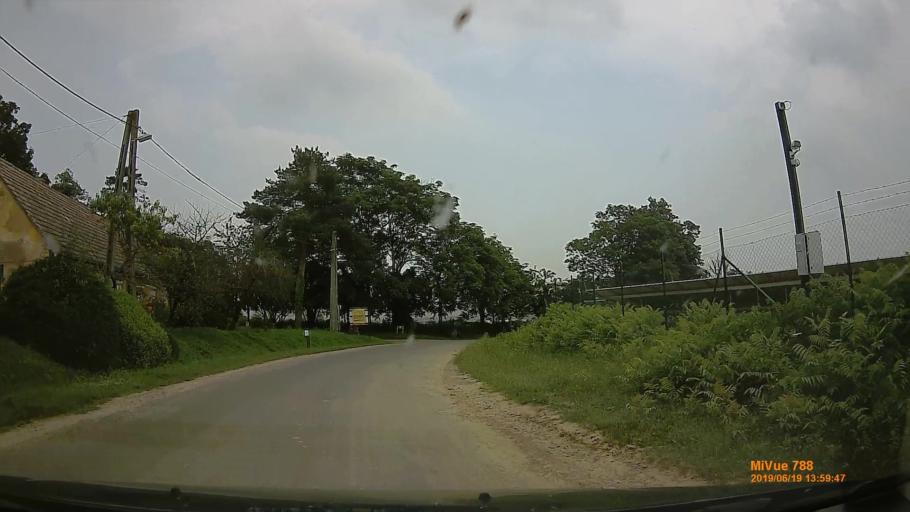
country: HU
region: Baranya
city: Szigetvar
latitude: 46.0871
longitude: 17.7990
